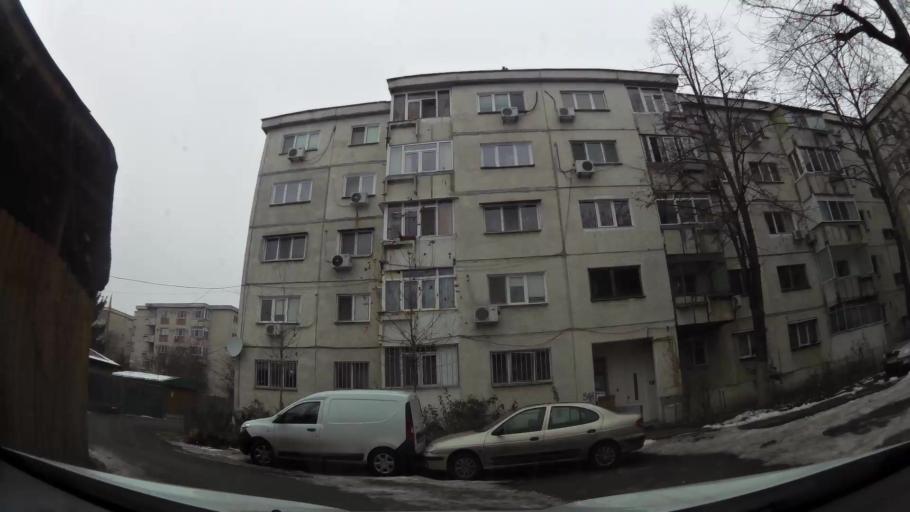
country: RO
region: Ilfov
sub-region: Comuna Chiajna
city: Rosu
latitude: 44.4403
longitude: 26.0195
